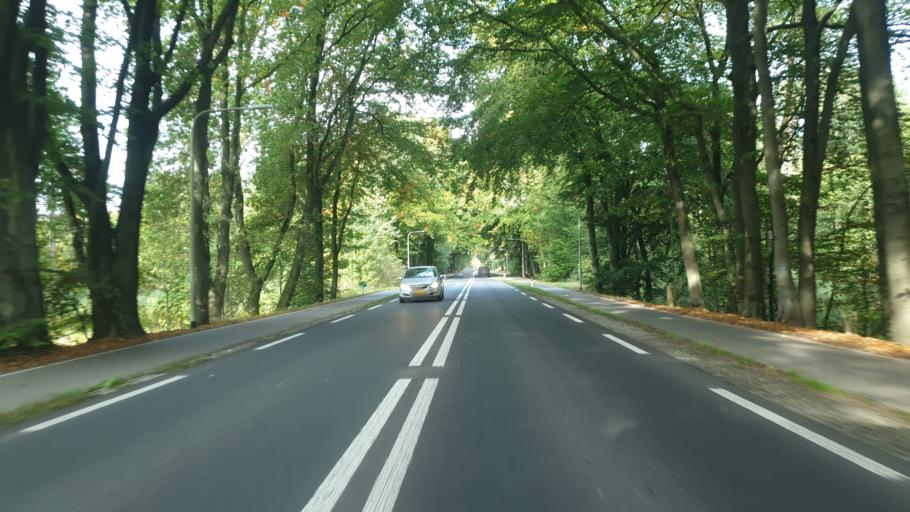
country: NL
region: Gelderland
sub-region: Gemeente Groesbeek
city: Berg en Dal
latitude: 51.7991
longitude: 5.9034
